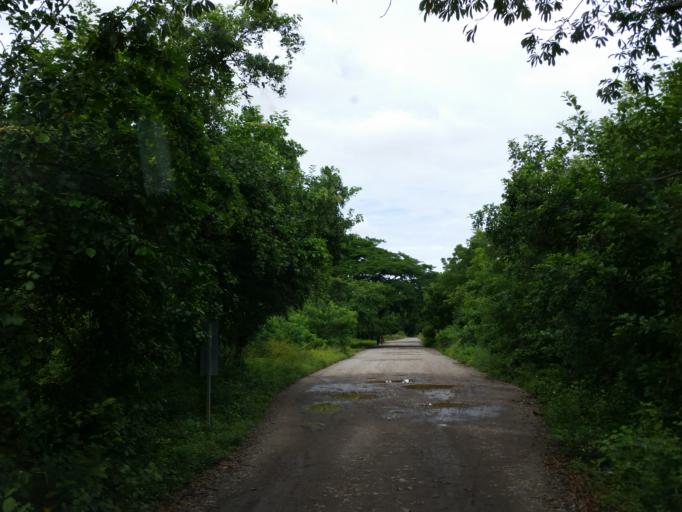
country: NI
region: Leon
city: Telica
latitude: 12.7146
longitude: -86.8748
